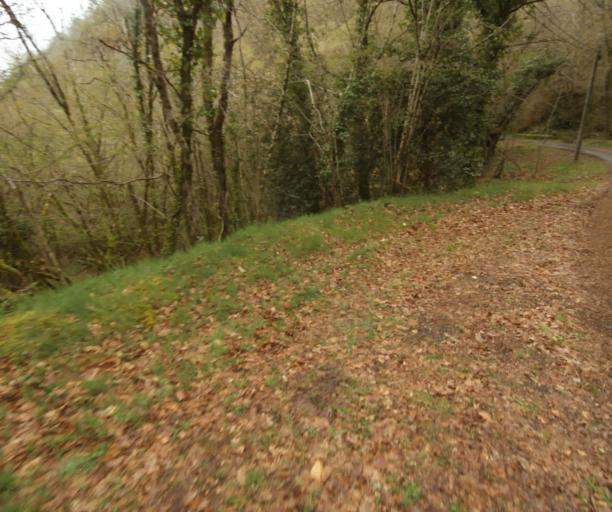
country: FR
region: Limousin
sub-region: Departement de la Correze
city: Saint-Privat
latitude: 45.2225
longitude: 2.0315
